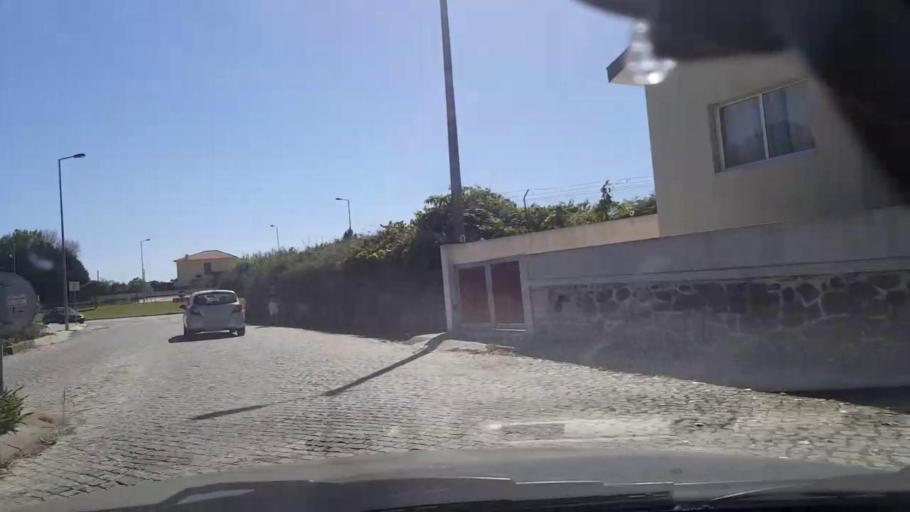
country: PT
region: Porto
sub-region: Vila do Conde
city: Arvore
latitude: 41.3182
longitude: -8.7233
